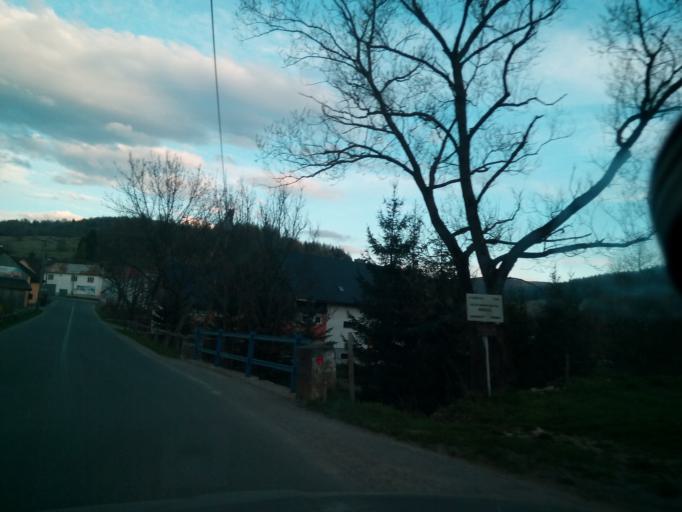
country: SK
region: Presovsky
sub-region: Okres Poprad
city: Zdiar
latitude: 49.2986
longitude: 20.3785
